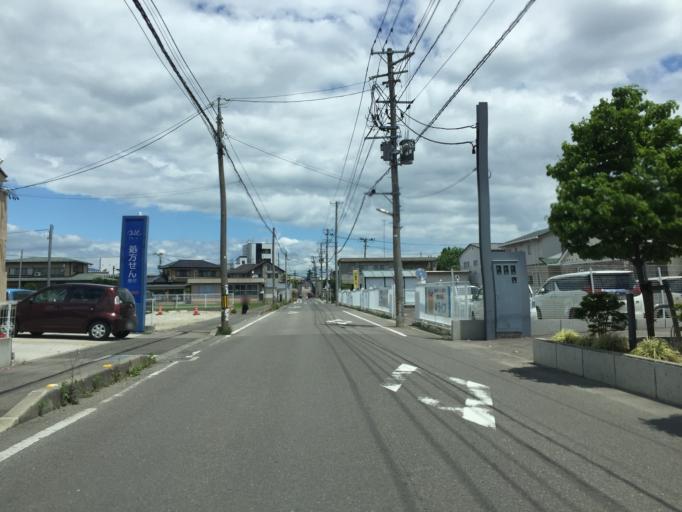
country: JP
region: Fukushima
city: Fukushima-shi
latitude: 37.7703
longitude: 140.4881
